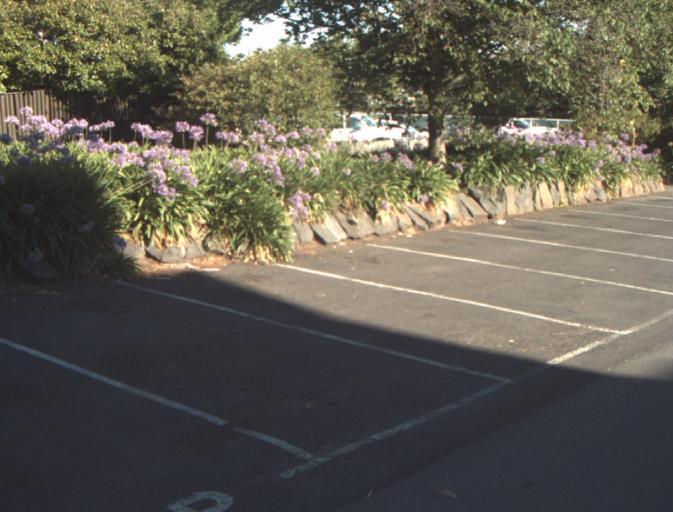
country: AU
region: Tasmania
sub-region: Launceston
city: East Launceston
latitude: -41.4334
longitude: 147.1474
